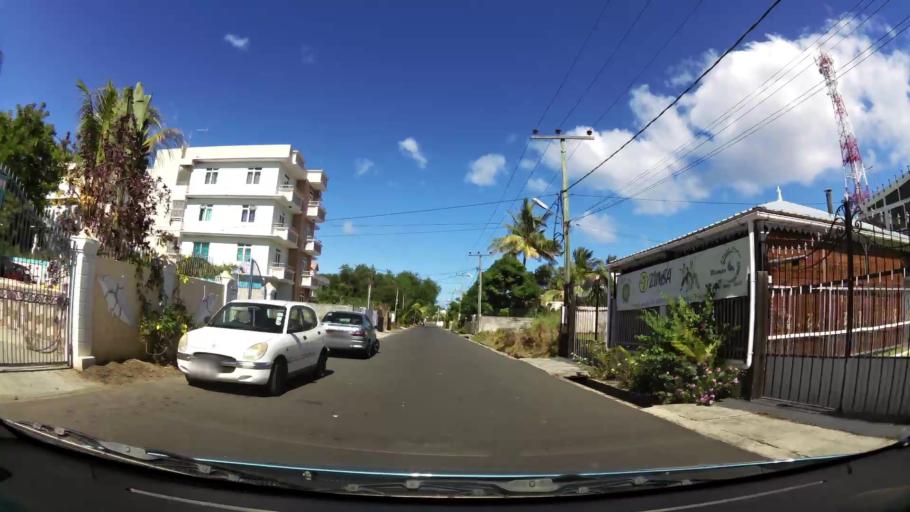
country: MU
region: Black River
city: Flic en Flac
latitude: -20.2909
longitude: 57.3661
